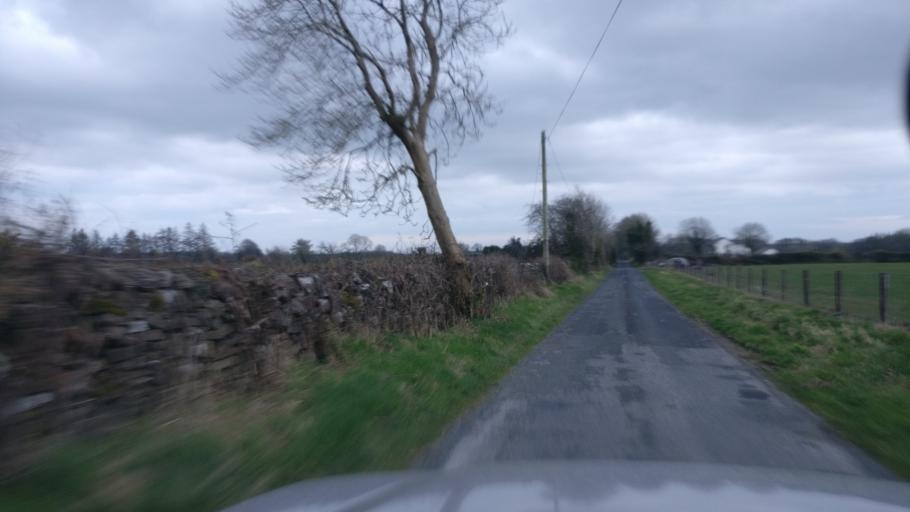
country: IE
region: Connaught
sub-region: County Galway
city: Loughrea
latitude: 53.2652
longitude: -8.4640
